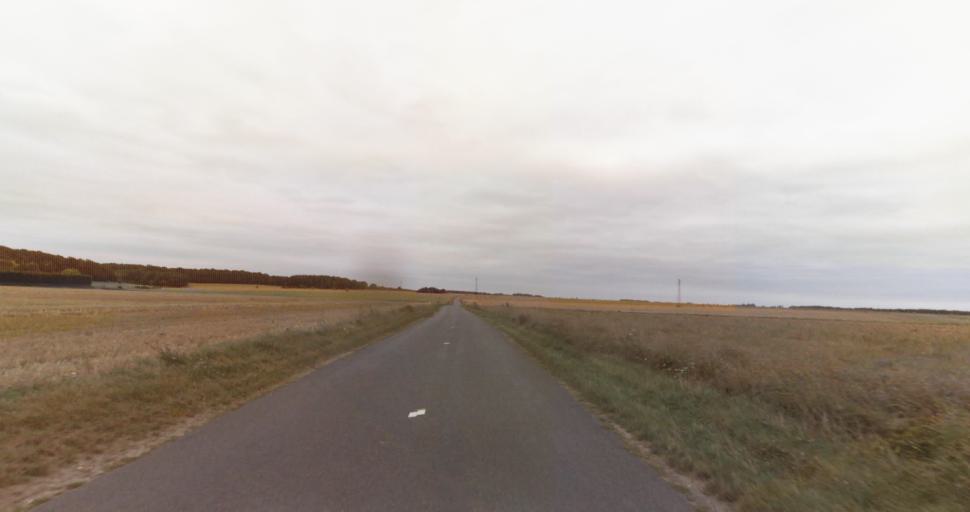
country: FR
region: Haute-Normandie
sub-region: Departement de l'Eure
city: Saint-Germain-sur-Avre
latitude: 48.7914
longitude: 1.2844
